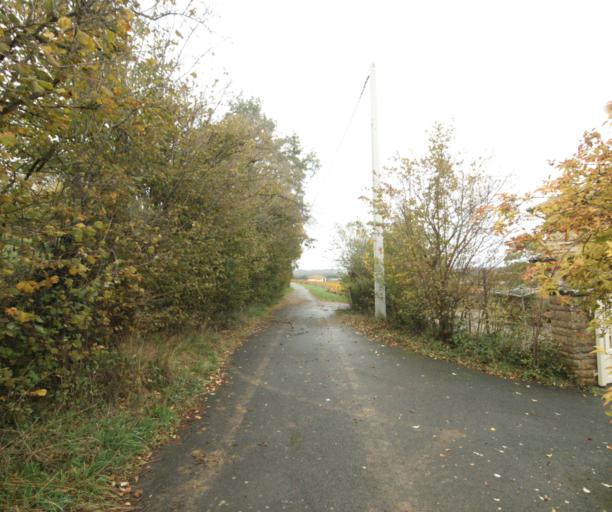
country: FR
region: Bourgogne
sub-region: Departement de Saone-et-Loire
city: Saint-Martin-Belle-Roche
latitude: 46.4670
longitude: 4.8468
